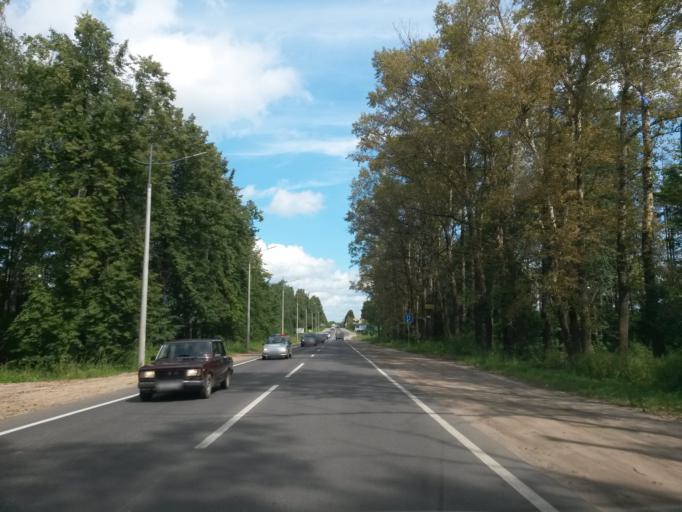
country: RU
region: Jaroslavl
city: Pereslavl'-Zalesskiy
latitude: 56.7583
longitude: 38.8676
